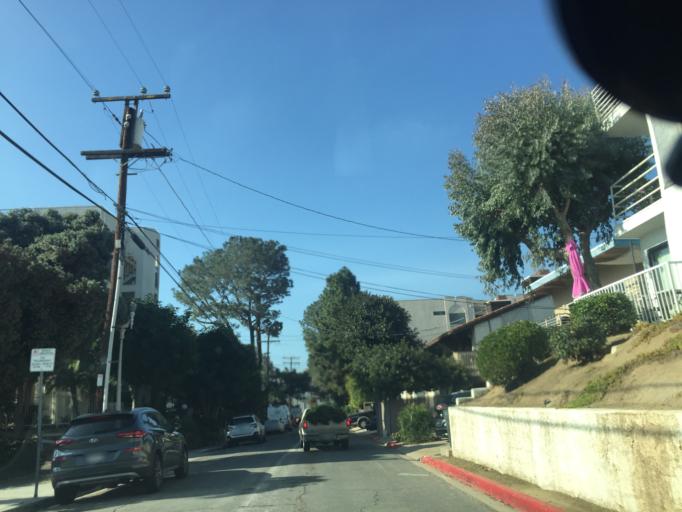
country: US
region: California
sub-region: San Diego County
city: La Jolla
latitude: 32.7925
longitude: -117.2447
